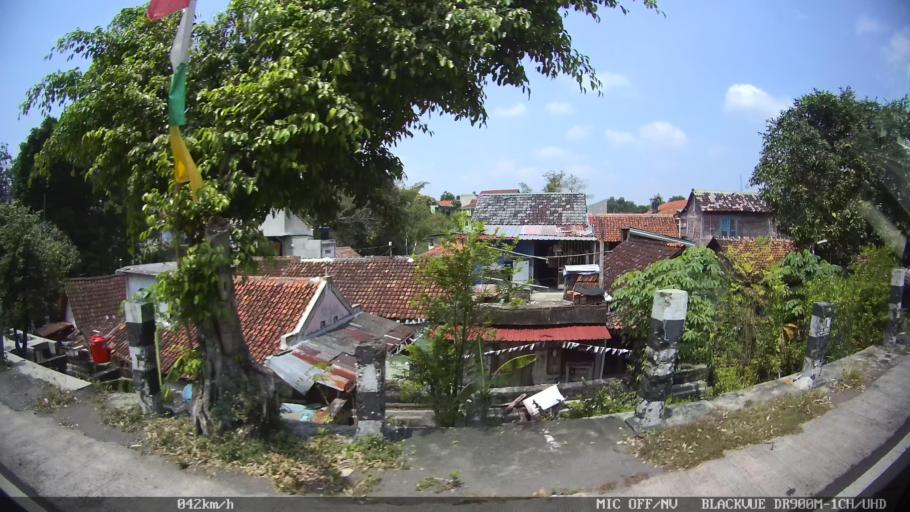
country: ID
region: Daerah Istimewa Yogyakarta
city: Yogyakarta
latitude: -7.8141
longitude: 110.3929
